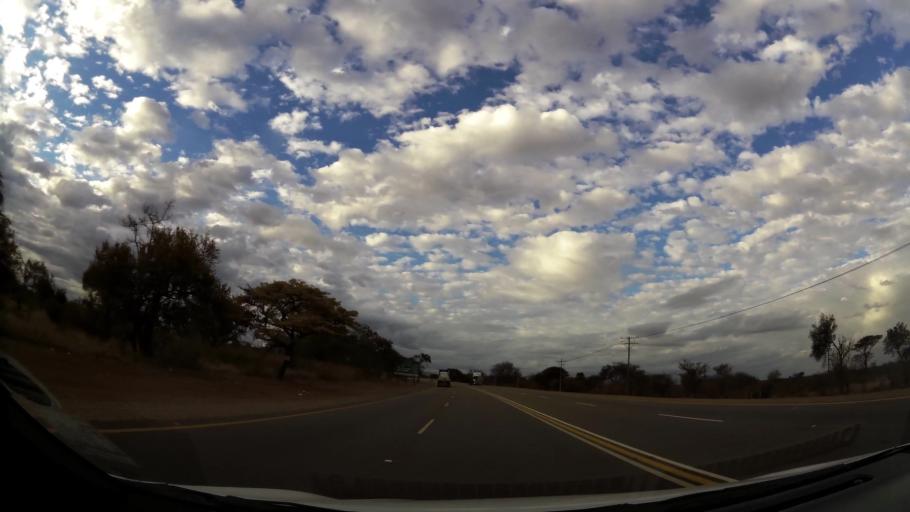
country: ZA
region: Limpopo
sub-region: Waterberg District Municipality
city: Modimolle
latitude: -24.5056
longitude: 28.7285
